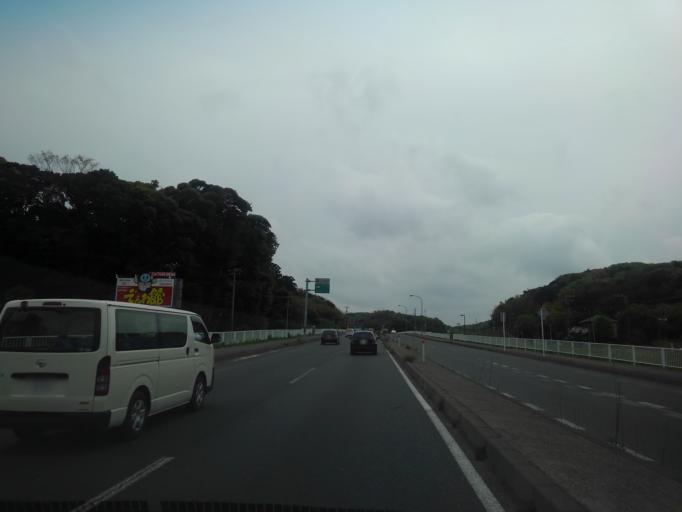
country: JP
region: Chiba
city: Kisarazu
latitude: 35.3557
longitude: 139.9207
